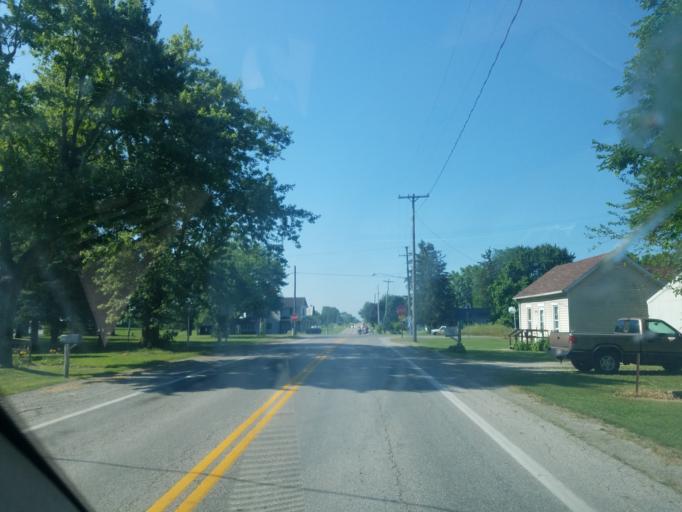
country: US
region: Ohio
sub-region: Union County
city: Richwood
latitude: 40.4085
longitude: -83.4531
